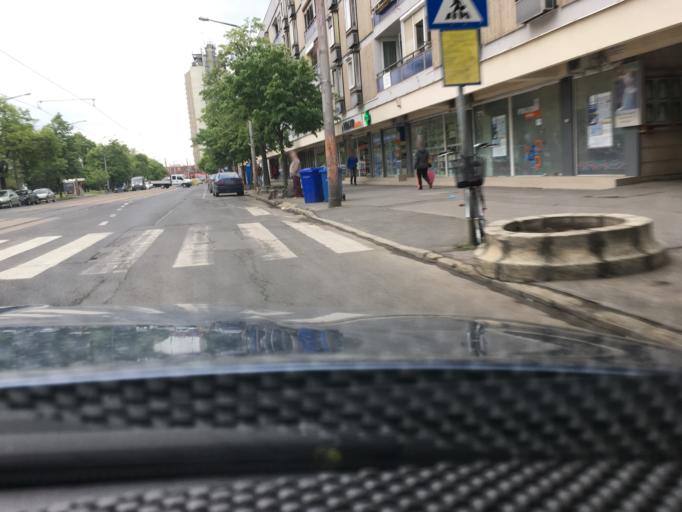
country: HU
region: Hajdu-Bihar
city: Debrecen
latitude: 47.5243
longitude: 21.6266
